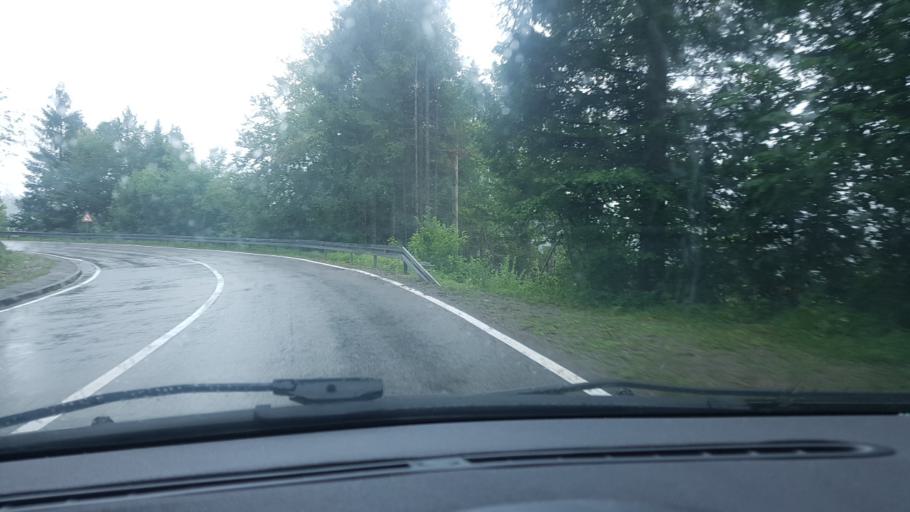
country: HR
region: Primorsko-Goranska
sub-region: Grad Delnice
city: Delnice
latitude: 45.3600
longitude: 14.7579
